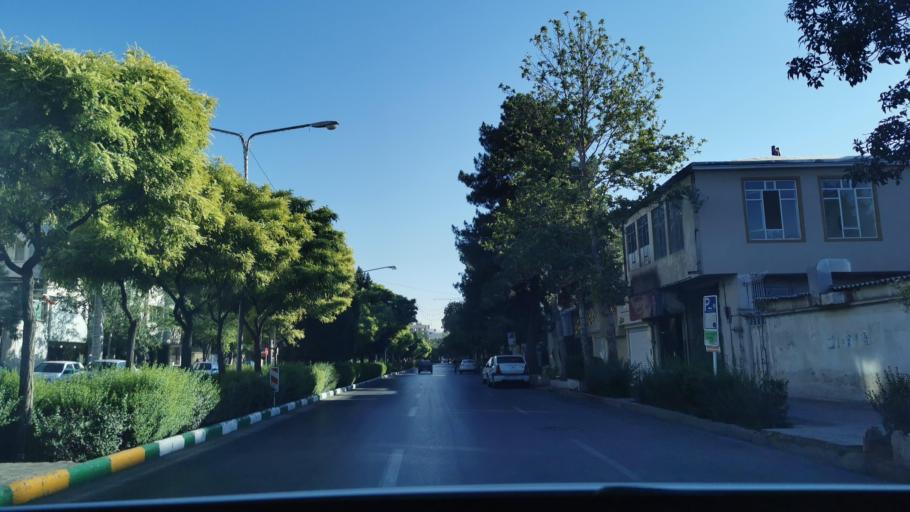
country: IR
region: Razavi Khorasan
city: Mashhad
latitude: 36.2951
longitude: 59.5685
